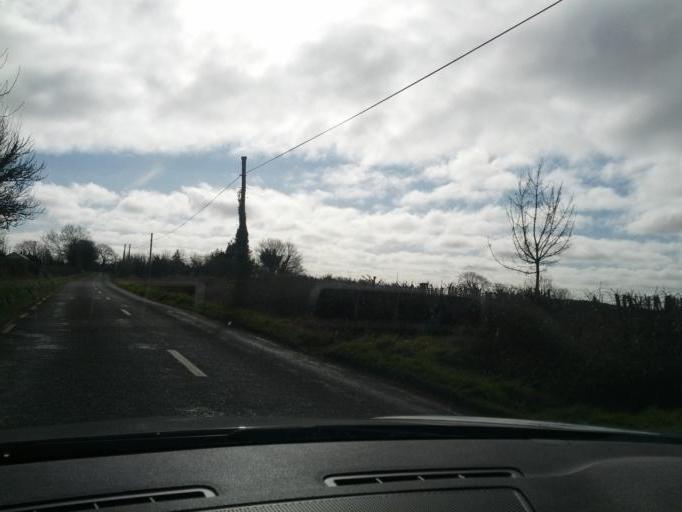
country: IE
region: Connaught
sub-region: County Galway
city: Ballinasloe
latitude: 53.4261
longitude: -8.4097
